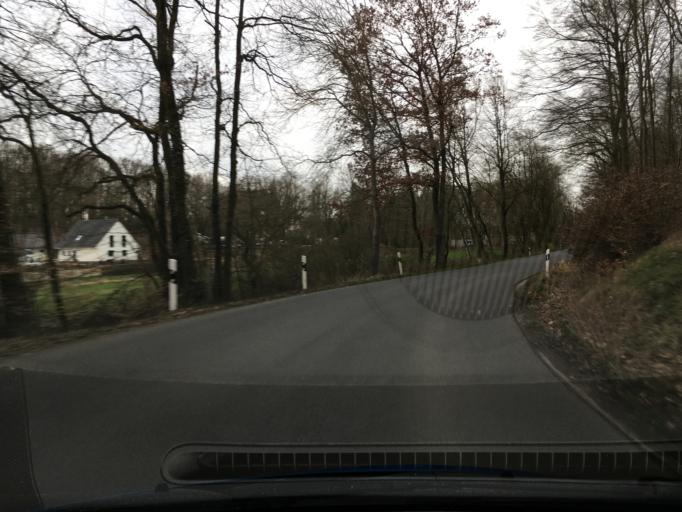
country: DE
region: Lower Saxony
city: Bad Bevensen
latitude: 53.0829
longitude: 10.5624
